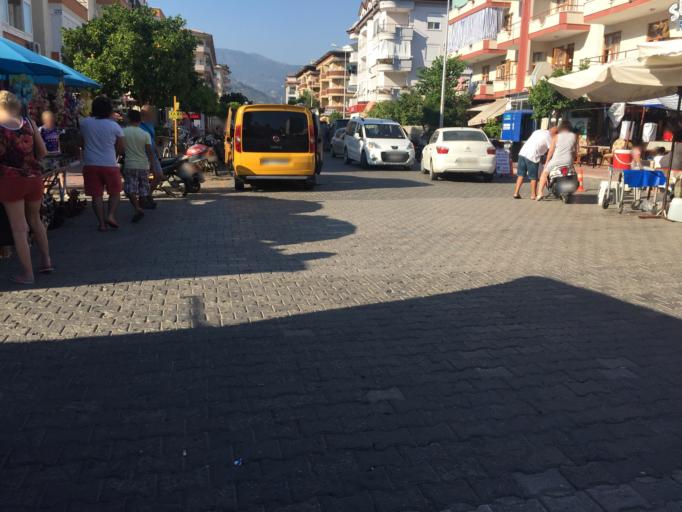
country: TR
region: Antalya
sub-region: Alanya
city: Alanya
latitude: 36.5367
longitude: 32.0383
